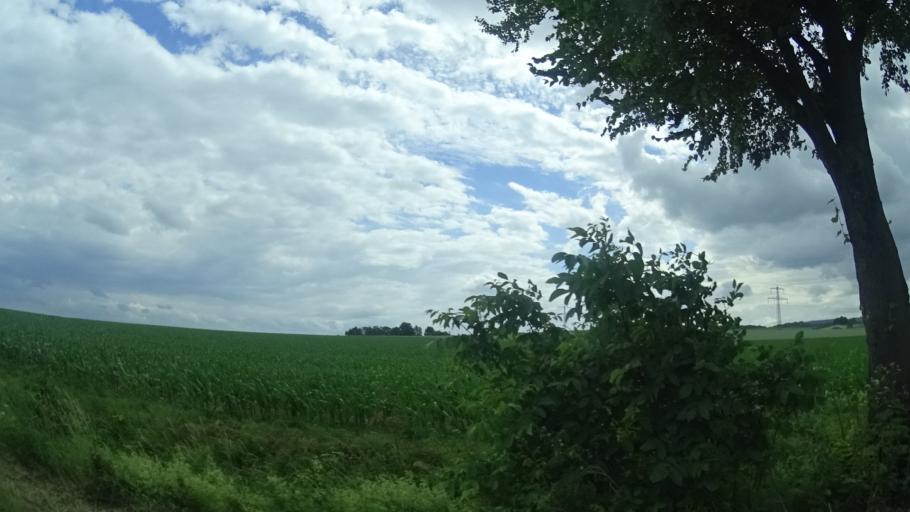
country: DE
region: Lower Saxony
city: Elze
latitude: 52.1554
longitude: 9.7314
